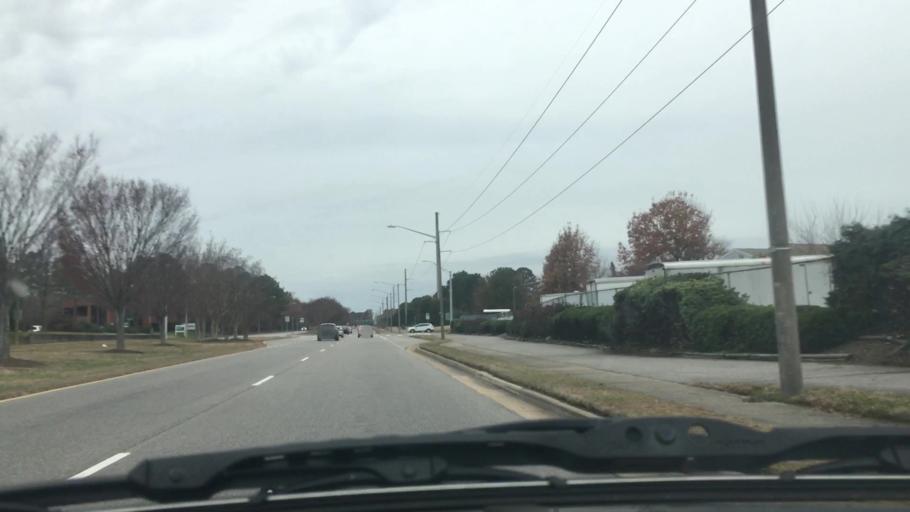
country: US
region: Virginia
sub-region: City of Virginia Beach
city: Virginia Beach
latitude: 36.8080
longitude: -76.1189
